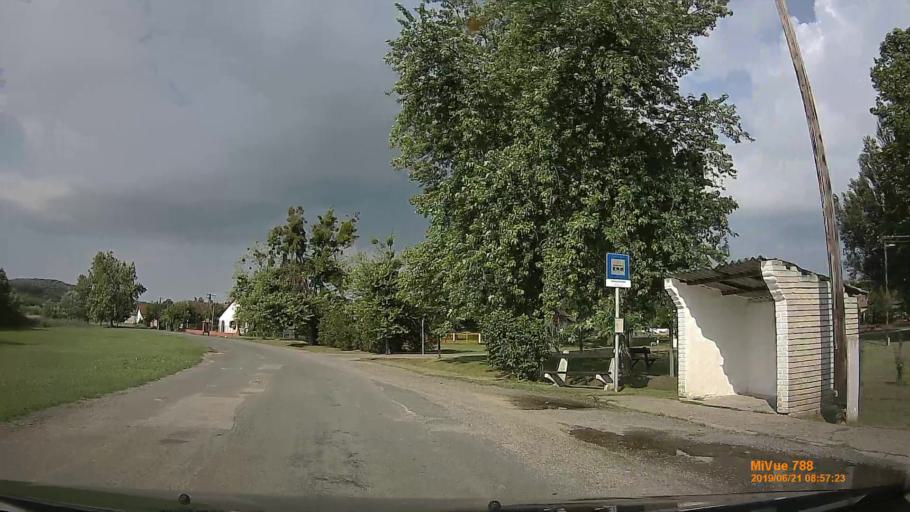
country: HU
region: Baranya
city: Szigetvar
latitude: 46.1528
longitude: 17.8672
